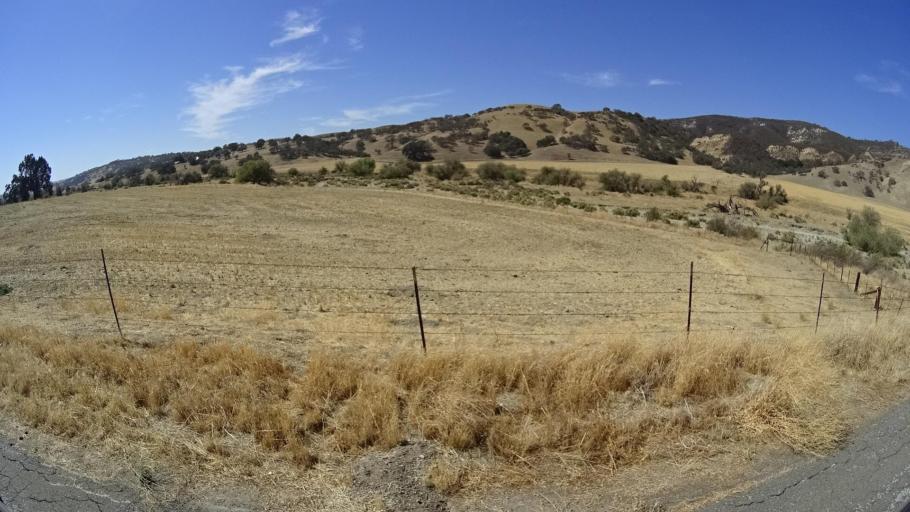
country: US
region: California
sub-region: San Luis Obispo County
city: San Miguel
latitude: 35.9400
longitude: -120.6722
